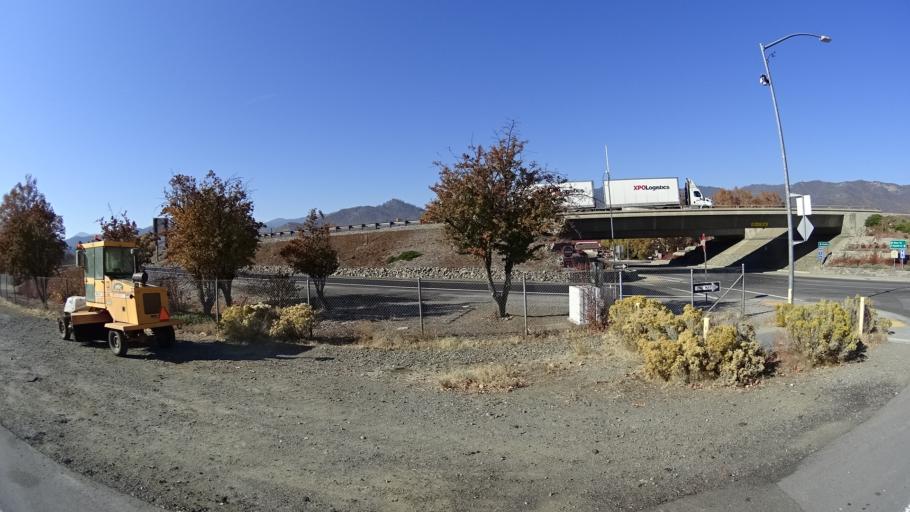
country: US
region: California
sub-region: Siskiyou County
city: Yreka
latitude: 41.7306
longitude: -122.6324
